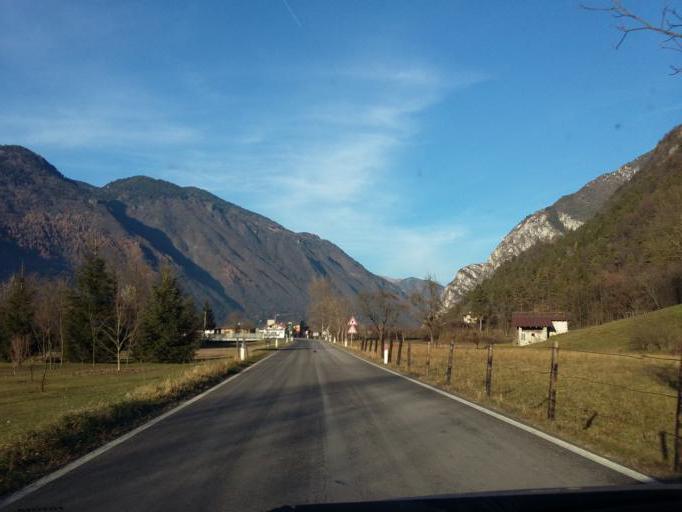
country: IT
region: Trentino-Alto Adige
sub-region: Provincia di Trento
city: Storo
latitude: 45.8361
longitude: 10.5653
